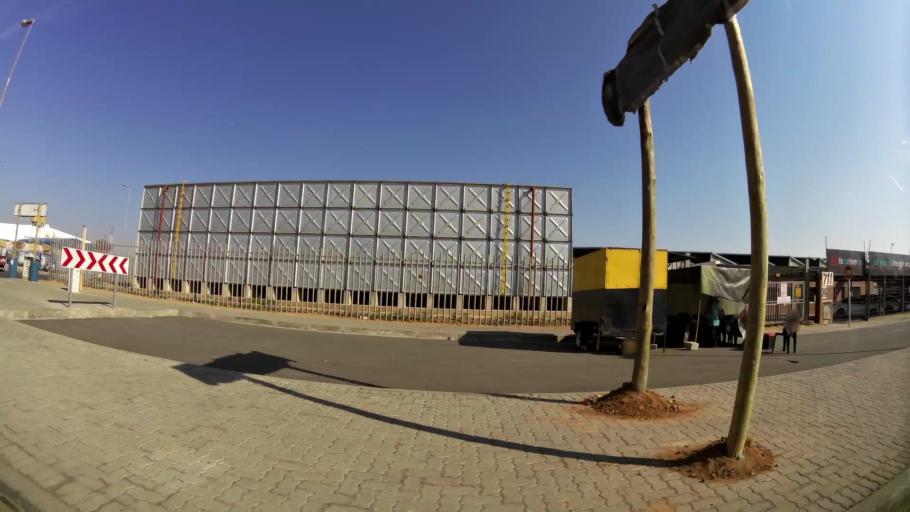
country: ZA
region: Gauteng
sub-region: City of Johannesburg Metropolitan Municipality
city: Modderfontein
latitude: -26.1009
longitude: 28.0855
